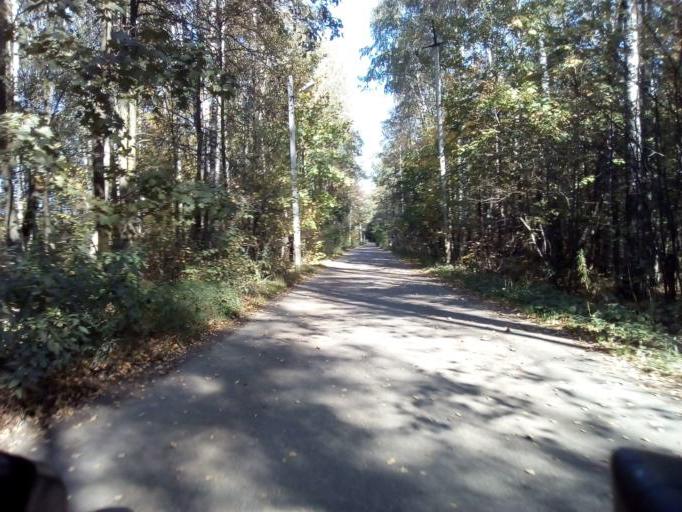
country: RU
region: Moskovskaya
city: Malyshevo
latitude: 55.5484
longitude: 38.3029
